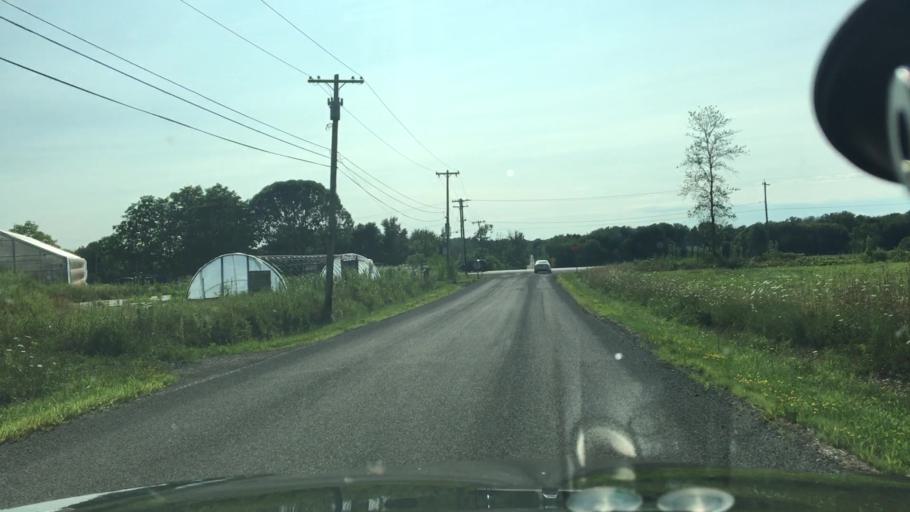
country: US
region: New York
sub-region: Erie County
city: North Collins
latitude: 42.6198
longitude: -78.9275
